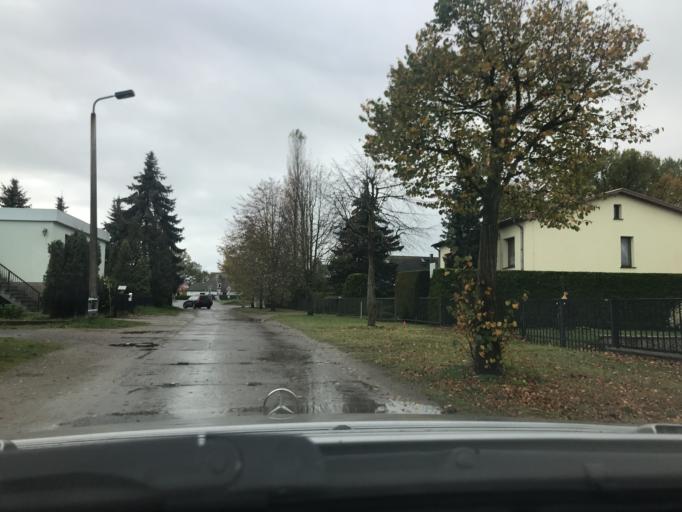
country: DE
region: Mecklenburg-Vorpommern
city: Ostseebad Zinnowitz
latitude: 54.0788
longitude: 13.8965
